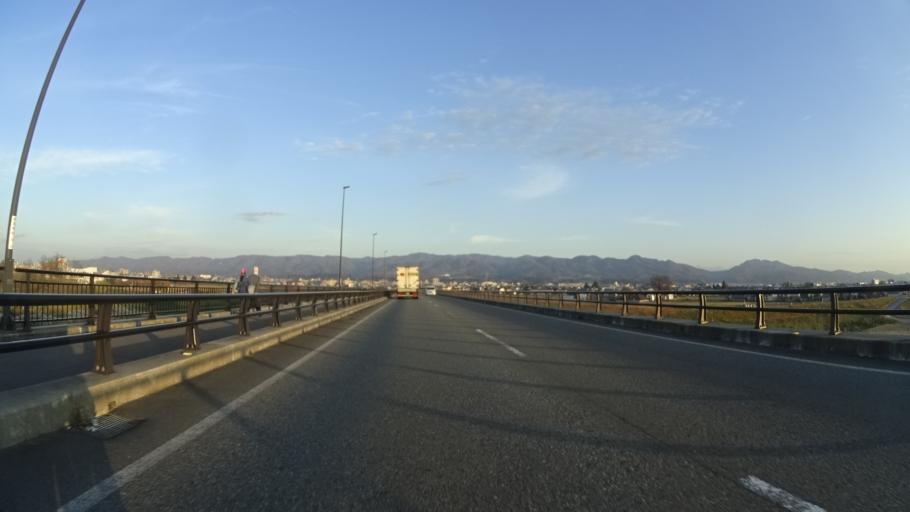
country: JP
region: Niigata
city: Nagaoka
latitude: 37.4302
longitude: 138.8244
